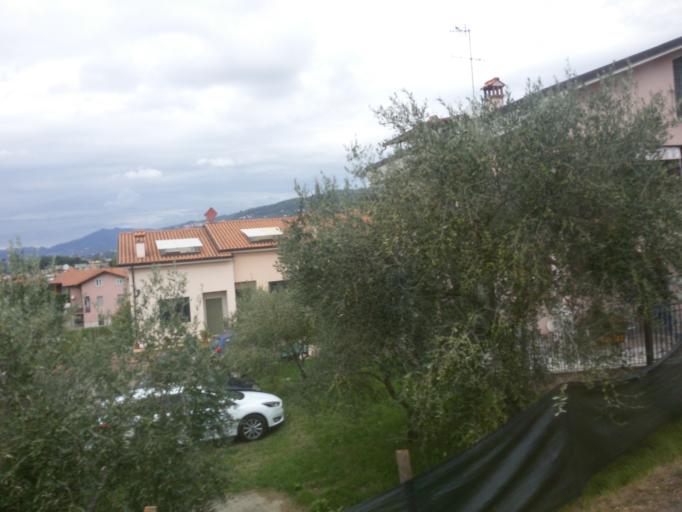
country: IT
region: Liguria
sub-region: Provincia di La Spezia
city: Santo Stefano di Magra
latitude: 44.1564
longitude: 9.9214
